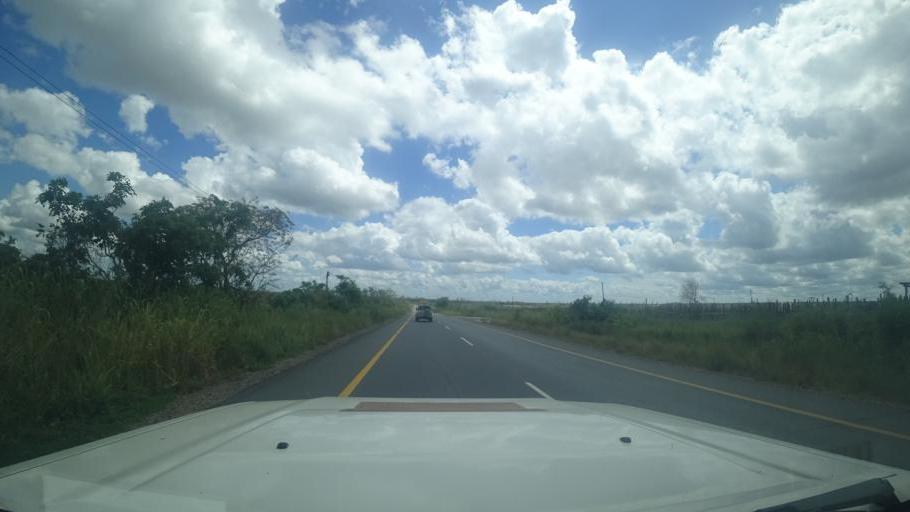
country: MZ
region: Sofala
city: Dondo
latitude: -19.5685
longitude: 34.6927
